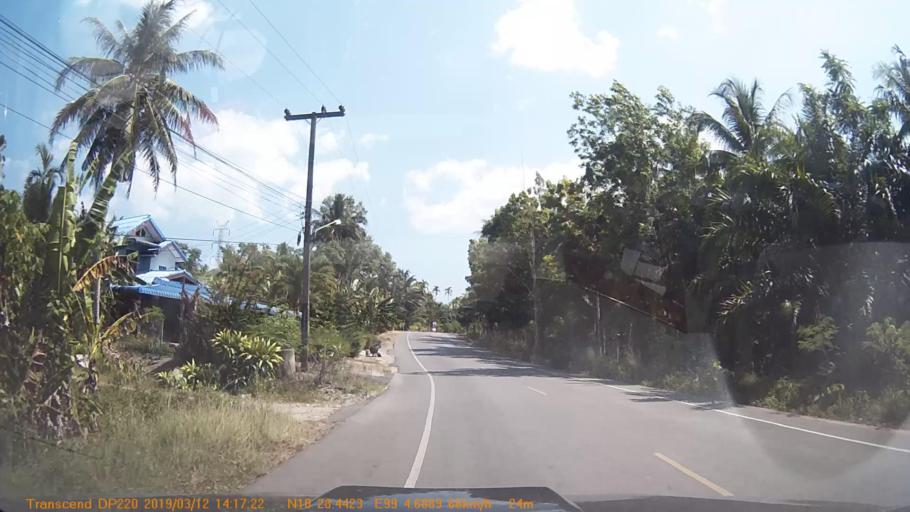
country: TH
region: Chumphon
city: Chumphon
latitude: 10.4739
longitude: 99.0781
